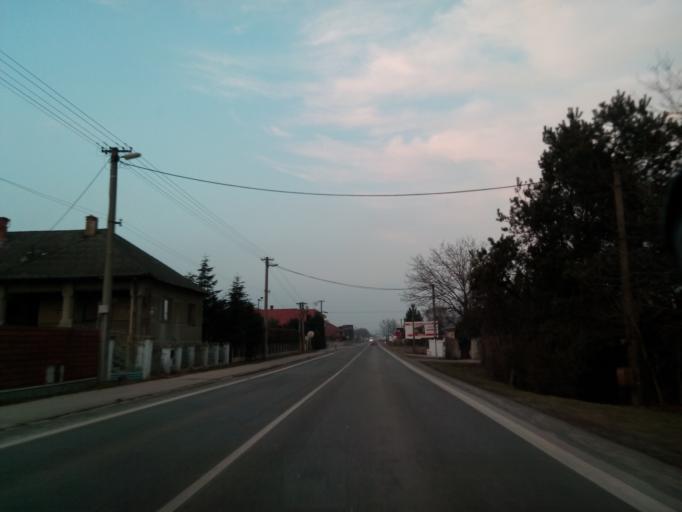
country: SK
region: Kosicky
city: Kosice
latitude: 48.6538
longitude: 21.2702
